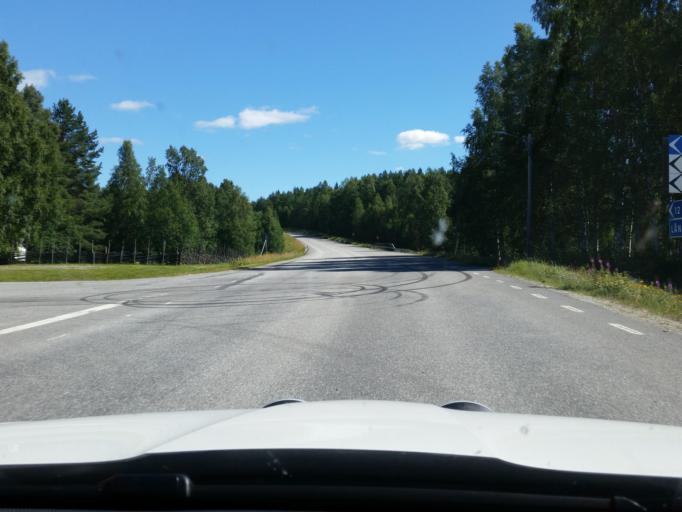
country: SE
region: Norrbotten
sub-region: Pitea Kommun
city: Roknas
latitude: 65.3181
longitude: 21.2479
